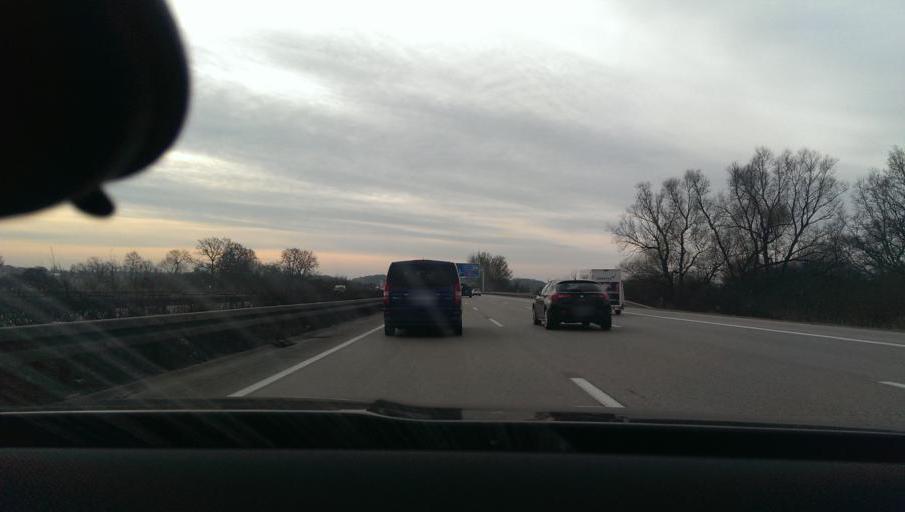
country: DE
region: Lower Saxony
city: Isernhagen Farster Bauerschaft
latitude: 52.4494
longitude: 9.8632
